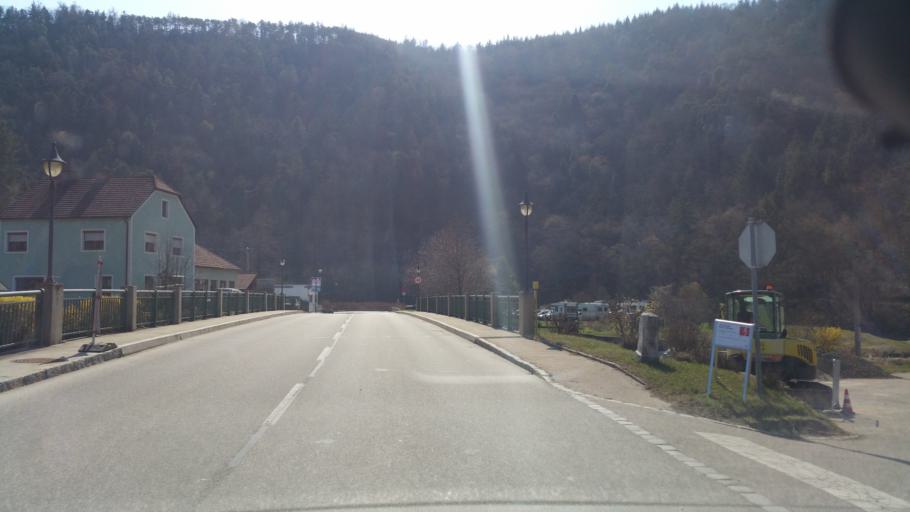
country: AT
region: Lower Austria
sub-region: Politischer Bezirk Krems
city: Senftenberg
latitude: 48.4458
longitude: 15.5591
